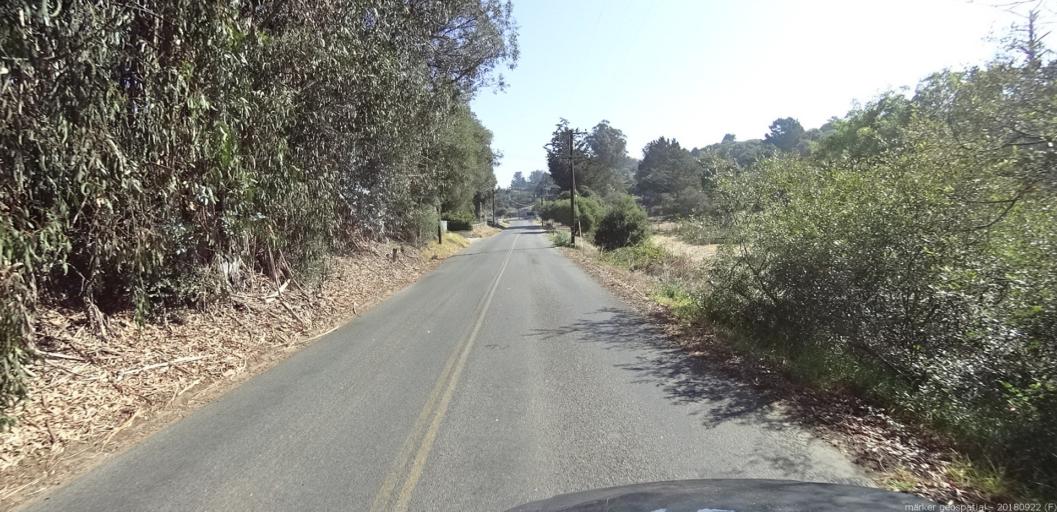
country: US
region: California
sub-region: Monterey County
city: Prunedale
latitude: 36.8054
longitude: -121.6659
